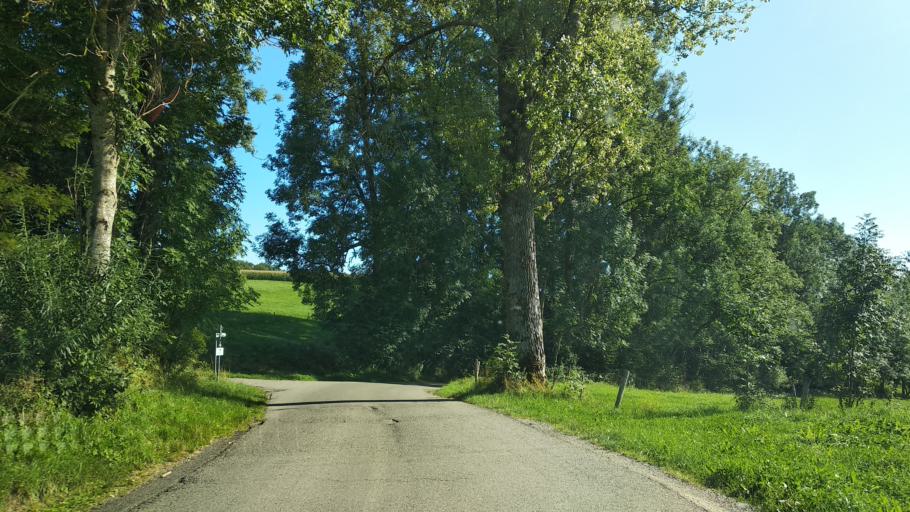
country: DE
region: Baden-Wuerttemberg
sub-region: Tuebingen Region
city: Leutkirch im Allgau
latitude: 47.8045
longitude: 10.0512
